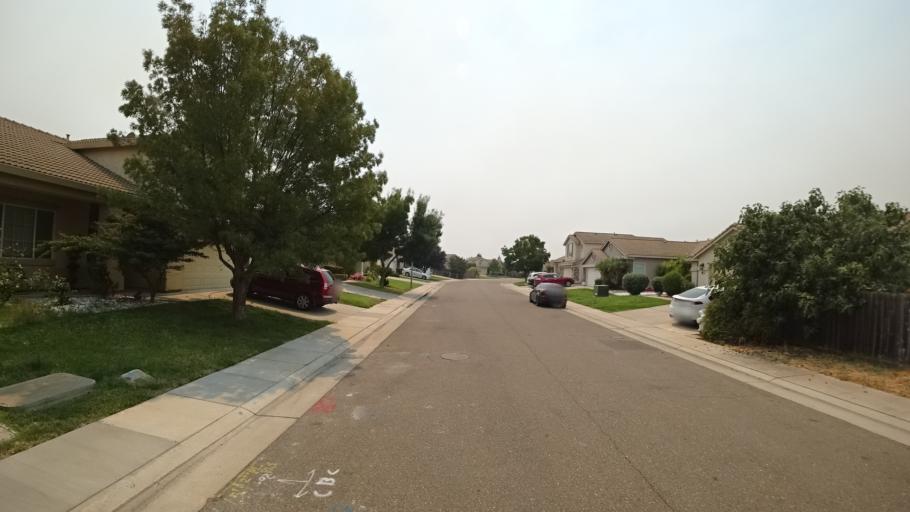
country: US
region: California
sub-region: Sacramento County
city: Laguna
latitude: 38.3963
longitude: -121.4198
